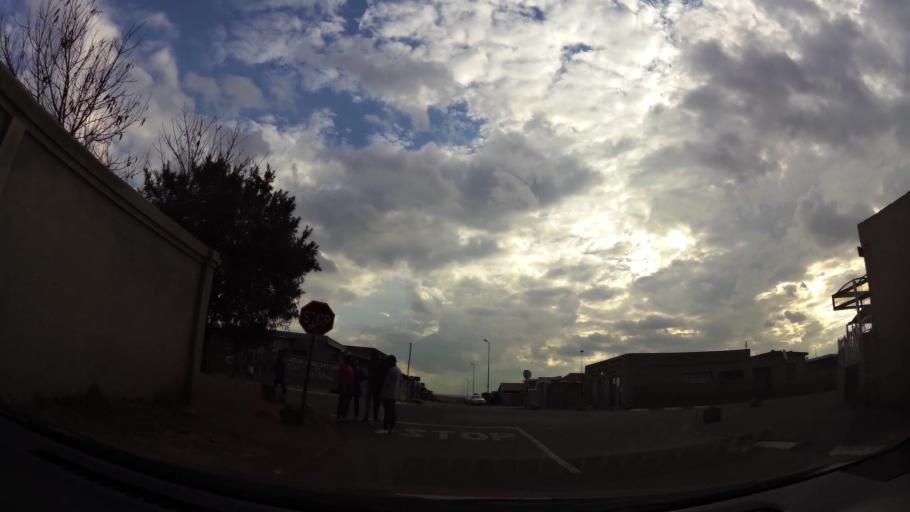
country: ZA
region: Gauteng
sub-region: City of Johannesburg Metropolitan Municipality
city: Soweto
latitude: -26.2433
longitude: 27.8160
